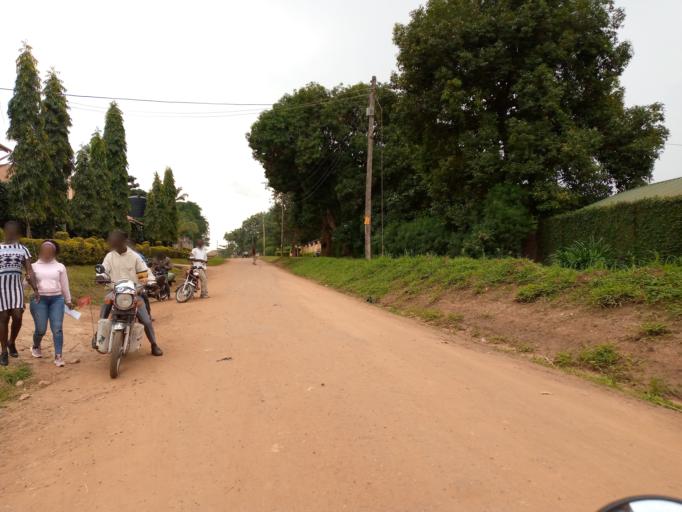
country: UG
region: Eastern Region
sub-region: Mbale District
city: Mbale
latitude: 1.0810
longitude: 34.1750
